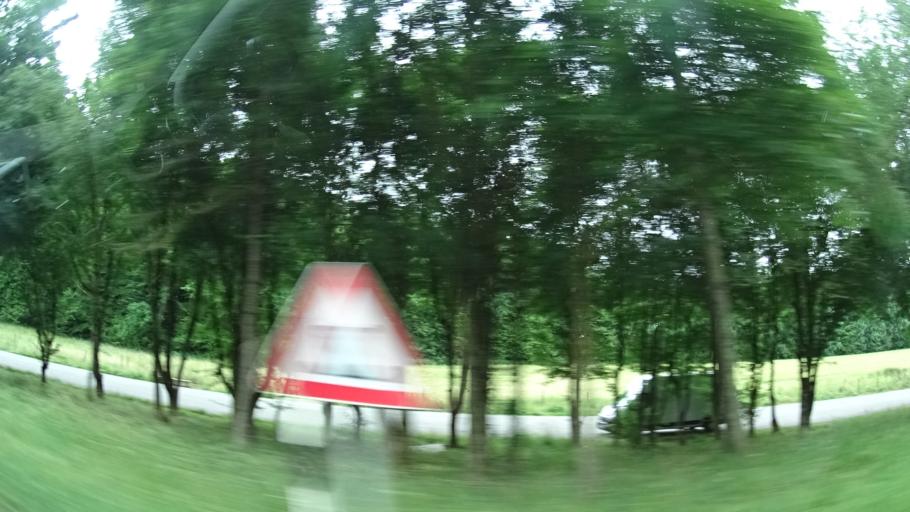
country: LU
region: Luxembourg
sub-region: Canton d'Esch-sur-Alzette
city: Bettembourg
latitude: 49.5052
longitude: 6.1294
